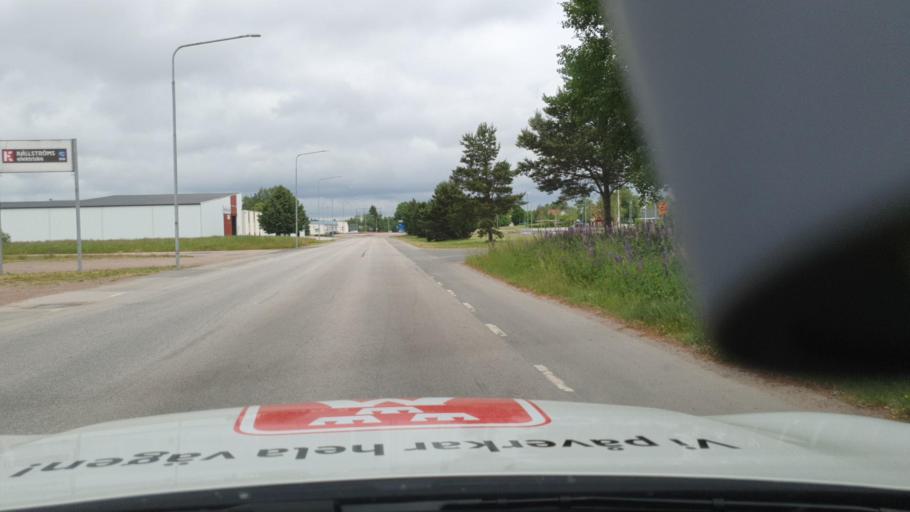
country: SE
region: Vaestra Goetaland
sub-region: Tibro Kommun
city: Tibro
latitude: 58.4116
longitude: 14.1534
